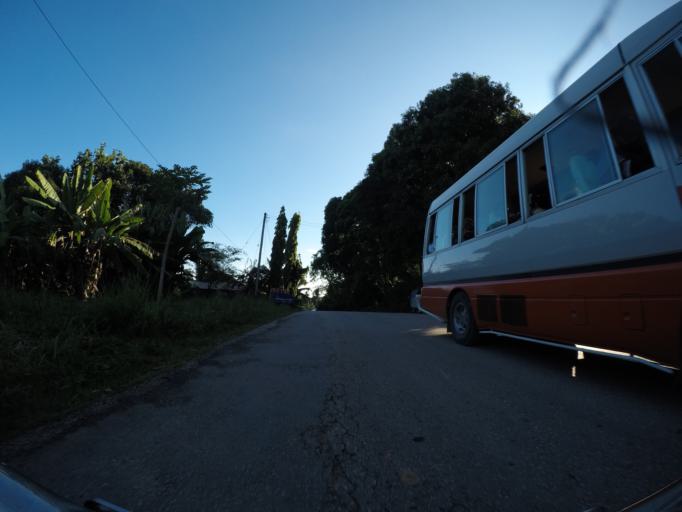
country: TZ
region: Pemba South
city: Mtambile
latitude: -5.3764
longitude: 39.7037
